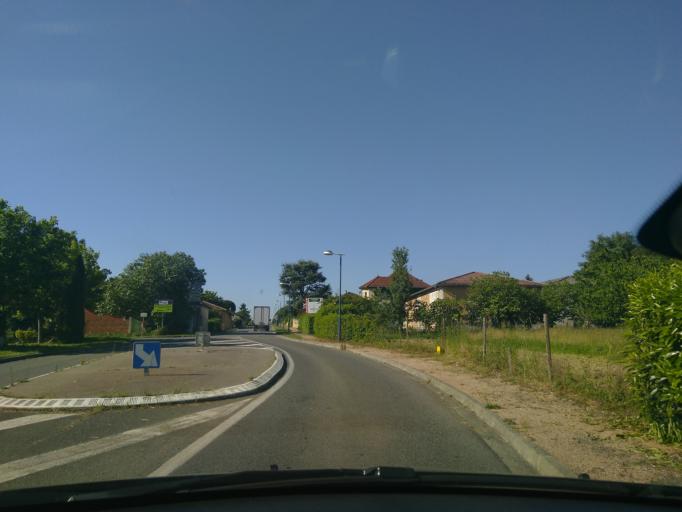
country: FR
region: Midi-Pyrenees
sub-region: Departement du Gers
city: Aubiet
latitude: 43.5274
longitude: 0.7641
